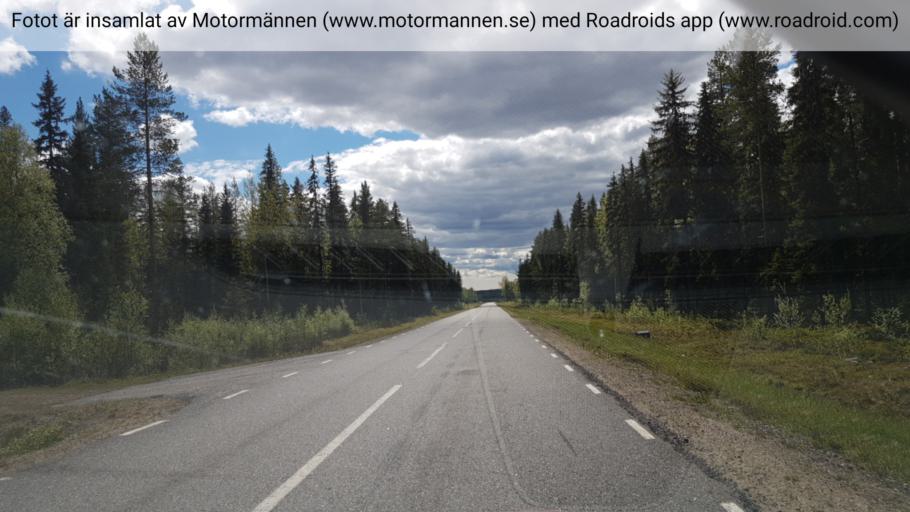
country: SE
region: Vaesterbotten
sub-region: Skelleftea Kommun
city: Langsele
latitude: 64.6675
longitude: 20.0189
